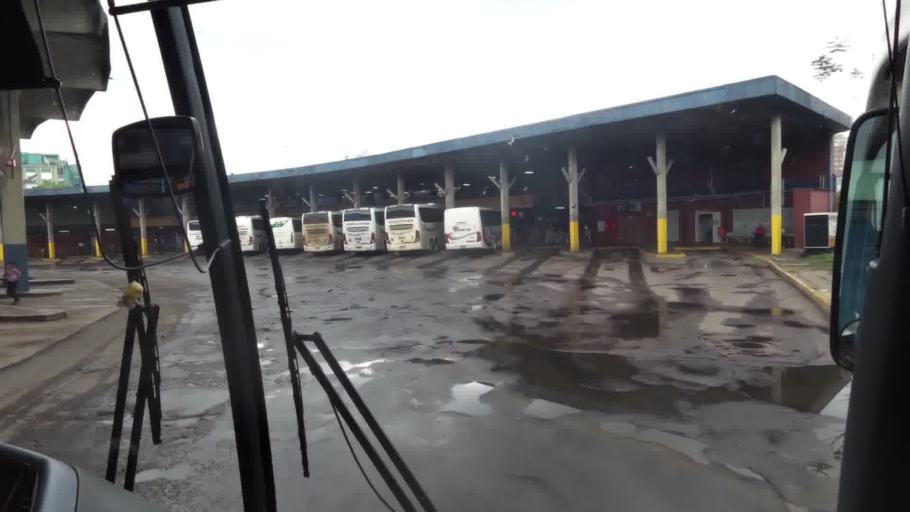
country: BR
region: Rio Grande do Sul
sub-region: Porto Alegre
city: Porto Alegre
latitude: -30.0231
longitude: -51.2200
